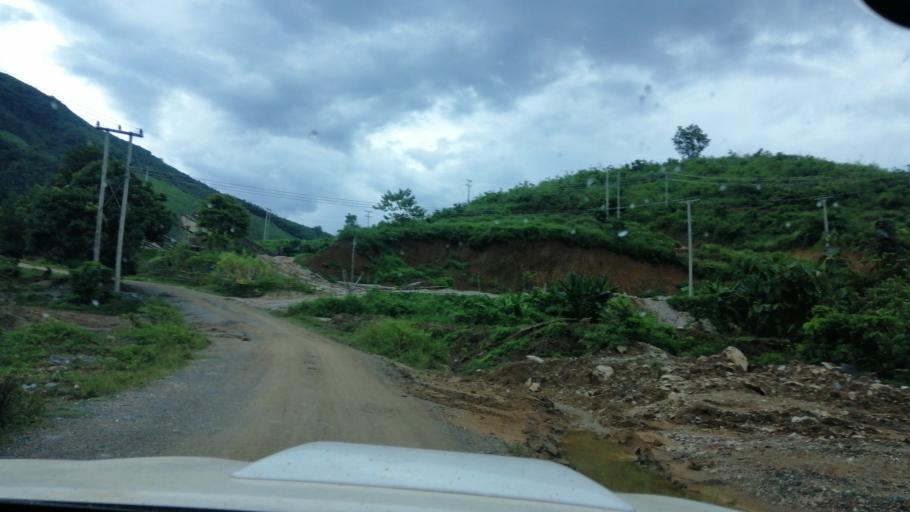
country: LA
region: Xiagnabouli
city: Sainyabuli
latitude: 19.1933
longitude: 101.7831
